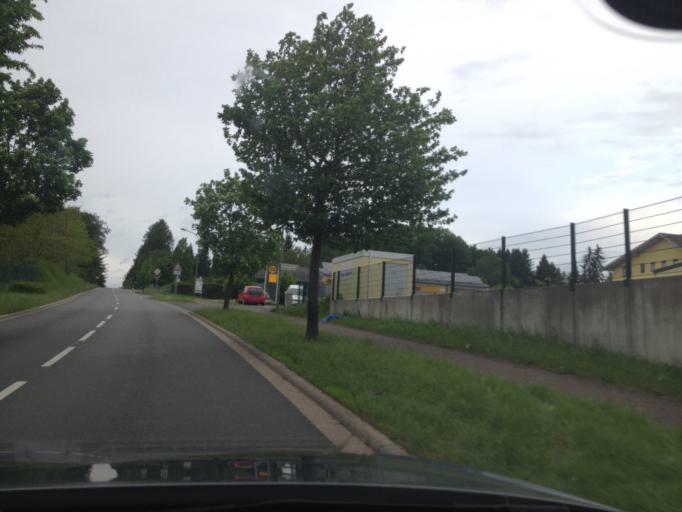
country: DE
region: Saarland
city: Kirkel
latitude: 49.2882
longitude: 7.2194
